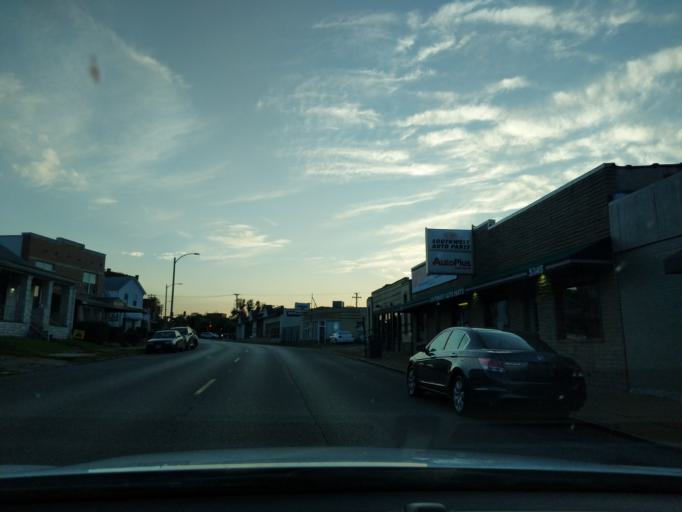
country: US
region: Missouri
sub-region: Saint Louis County
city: Richmond Heights
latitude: 38.6108
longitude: -90.2766
